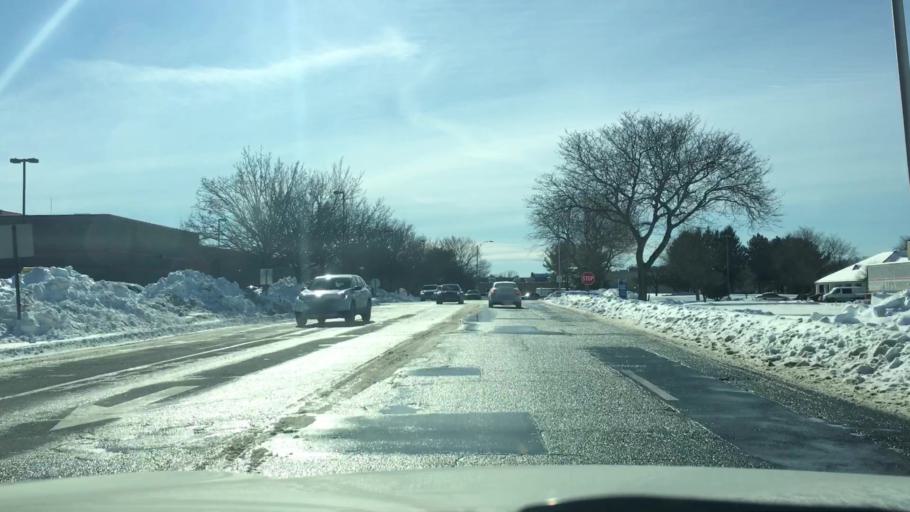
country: US
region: Massachusetts
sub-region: Hampden County
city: Chicopee
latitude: 42.1332
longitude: -72.6214
